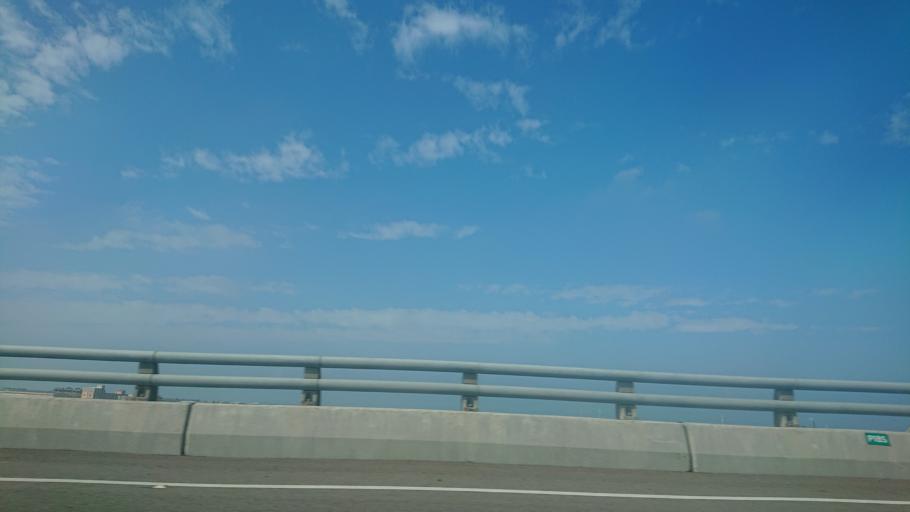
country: TW
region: Taiwan
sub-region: Changhua
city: Chang-hua
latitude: 24.0516
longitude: 120.4055
